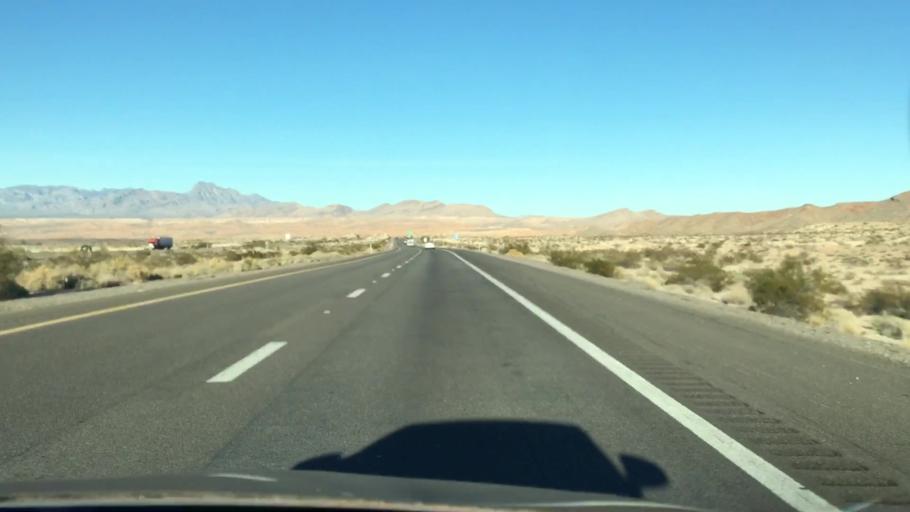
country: US
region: Nevada
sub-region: Clark County
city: Moapa Town
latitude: 36.6406
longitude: -114.5945
